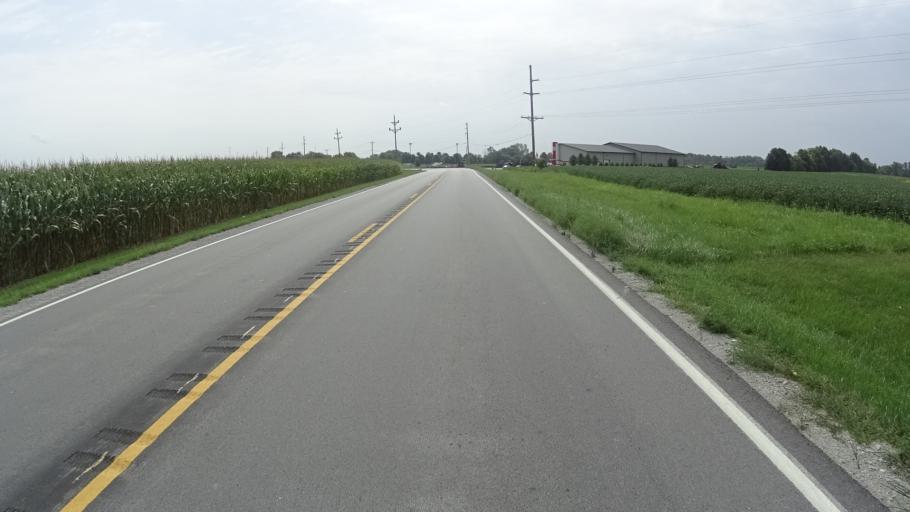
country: US
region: Indiana
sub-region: Madison County
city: Pendleton
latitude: 40.0073
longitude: -85.7836
